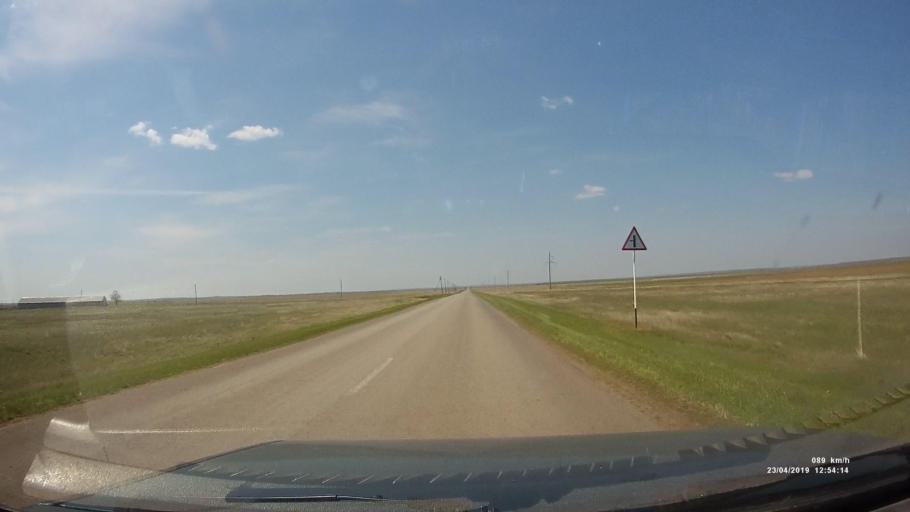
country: RU
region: Kalmykiya
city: Yashalta
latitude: 46.5790
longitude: 42.5809
